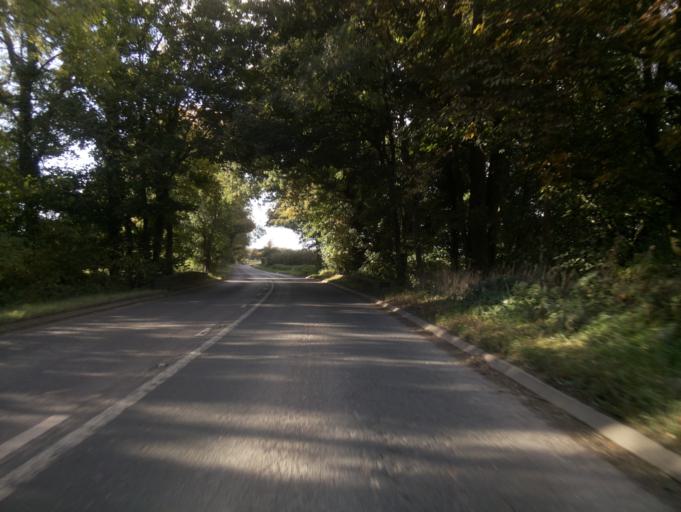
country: GB
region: England
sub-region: Herefordshire
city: Kinnersley
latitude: 52.1162
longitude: -2.9764
